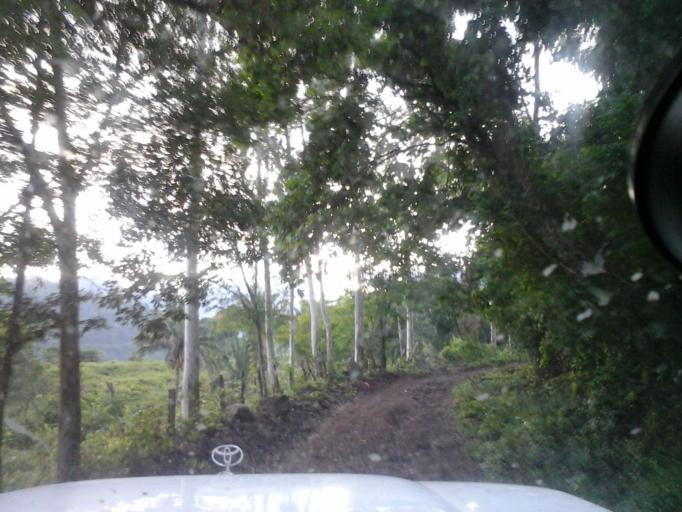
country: CO
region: Cesar
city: Agustin Codazzi
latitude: 10.1736
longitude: -73.1498
